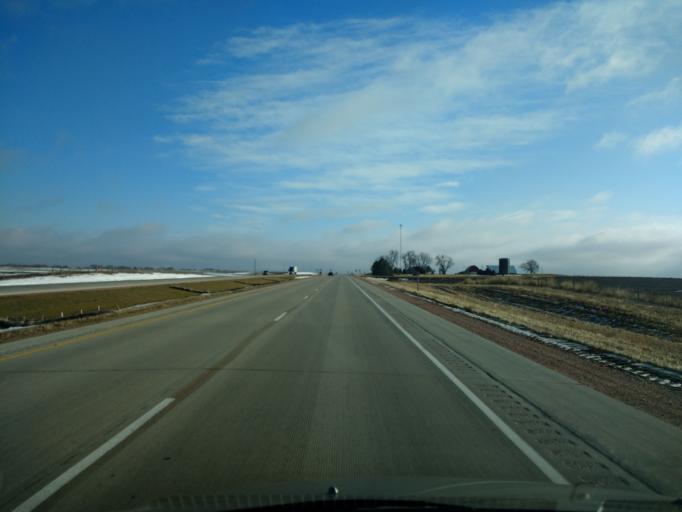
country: US
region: Iowa
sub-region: Ida County
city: Holstein
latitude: 42.4746
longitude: -95.5588
